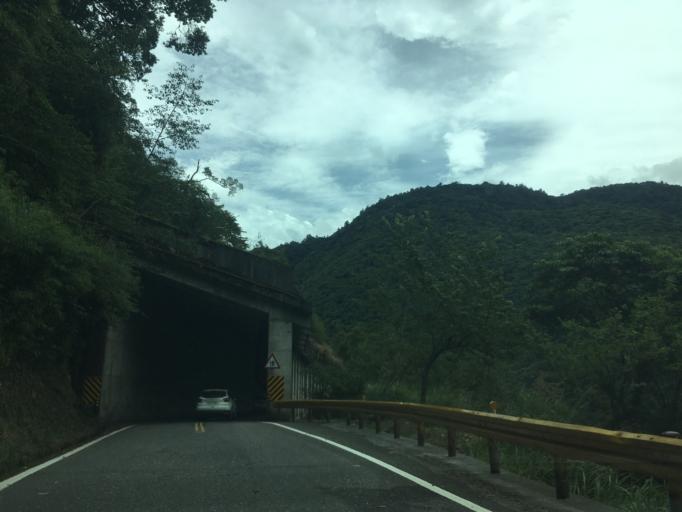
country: TW
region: Taiwan
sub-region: Hualien
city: Hualian
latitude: 24.1925
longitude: 121.4073
